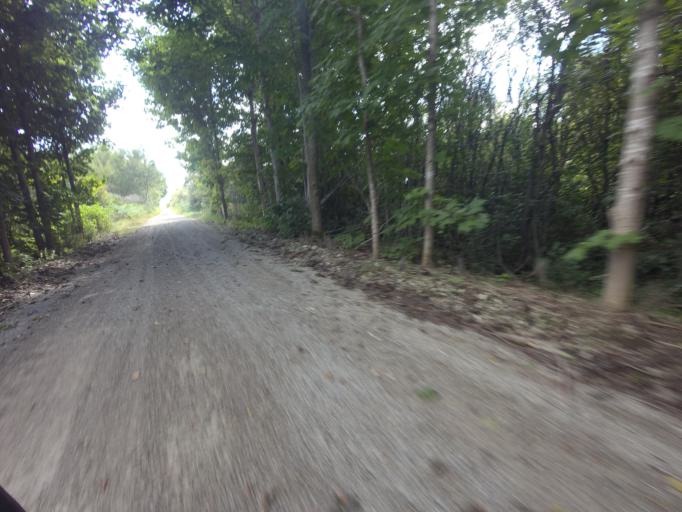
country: CA
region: Ontario
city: Huron East
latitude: 43.6471
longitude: -81.2191
